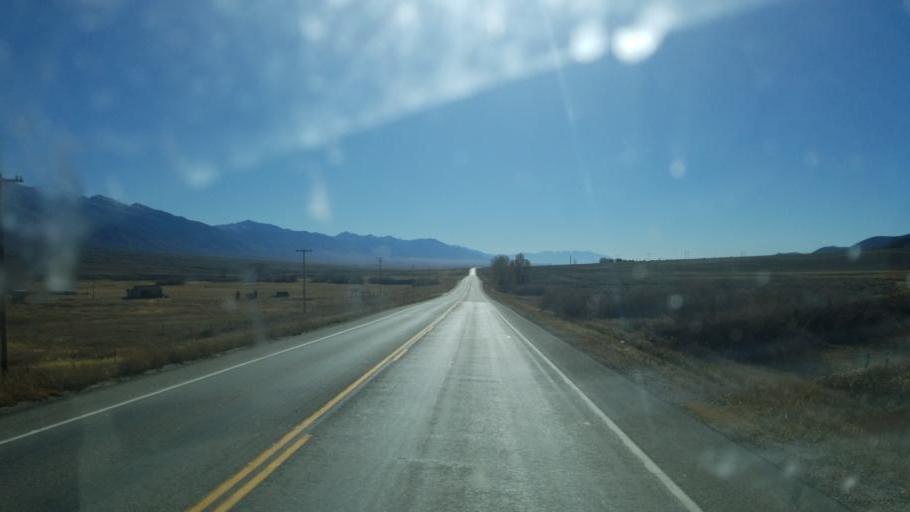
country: US
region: Colorado
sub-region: Chaffee County
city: Salida
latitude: 38.3843
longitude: -106.0530
